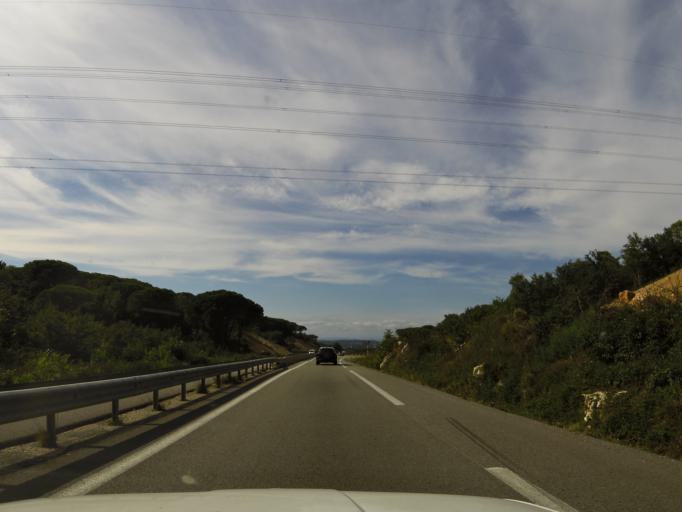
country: FR
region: Languedoc-Roussillon
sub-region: Departement du Gard
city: La Calmette
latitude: 43.9120
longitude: 4.2679
